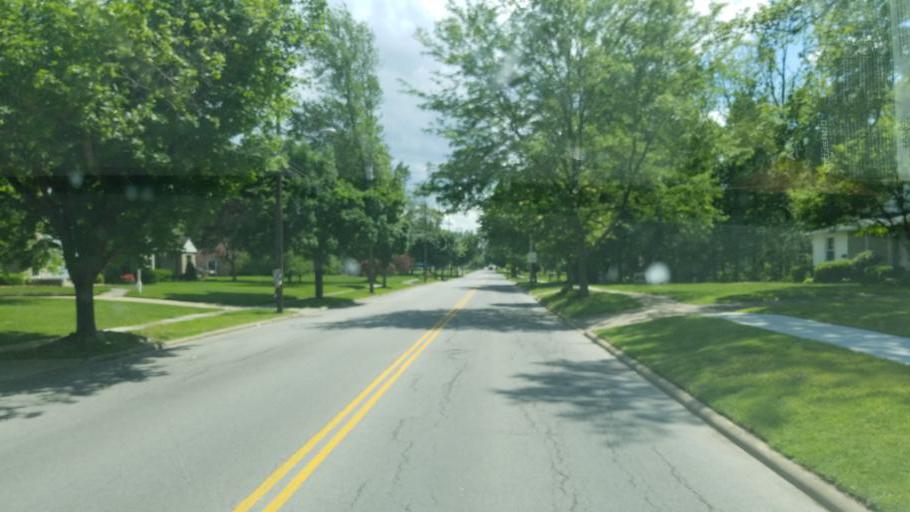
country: US
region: Ohio
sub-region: Huron County
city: Norwalk
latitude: 41.2331
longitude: -82.6164
